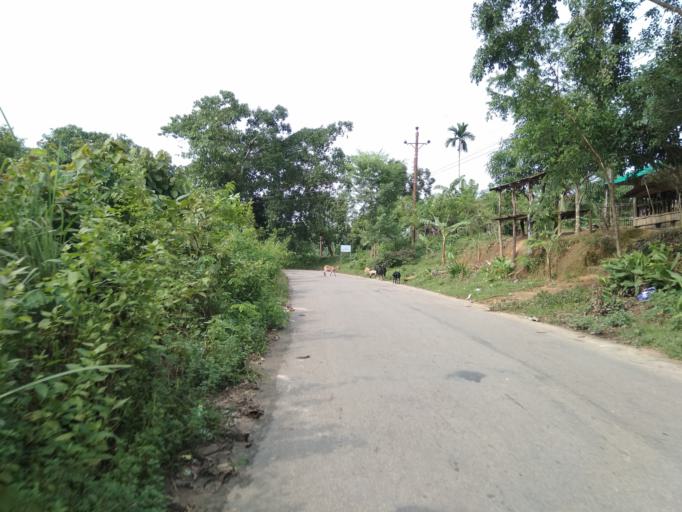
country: BD
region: Chittagong
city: Khagrachhari
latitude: 23.0098
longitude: 92.0108
